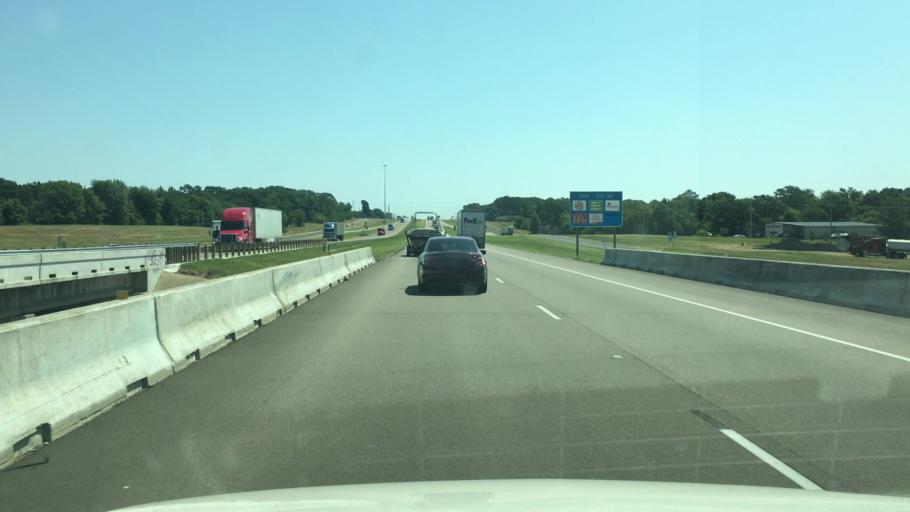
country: US
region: Texas
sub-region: Titus County
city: Mount Pleasant
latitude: 33.1695
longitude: -95.0001
